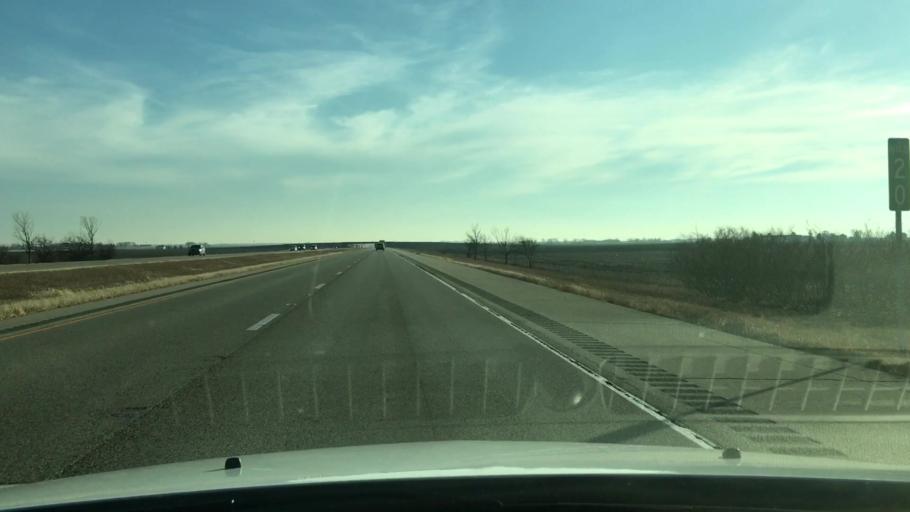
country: US
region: Illinois
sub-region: Woodford County
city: El Paso
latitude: 40.8202
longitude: -89.0361
